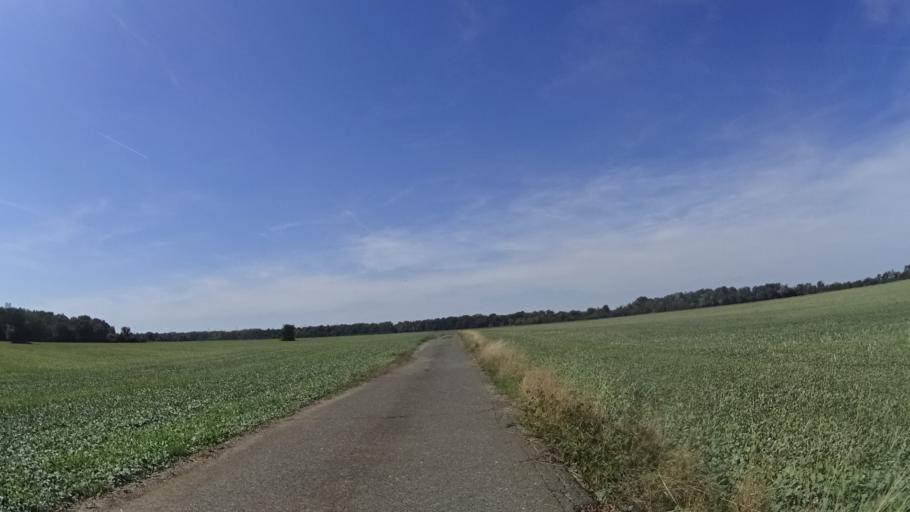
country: AT
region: Lower Austria
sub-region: Politischer Bezirk Ganserndorf
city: Angern an der March
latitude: 48.3638
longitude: 16.8700
